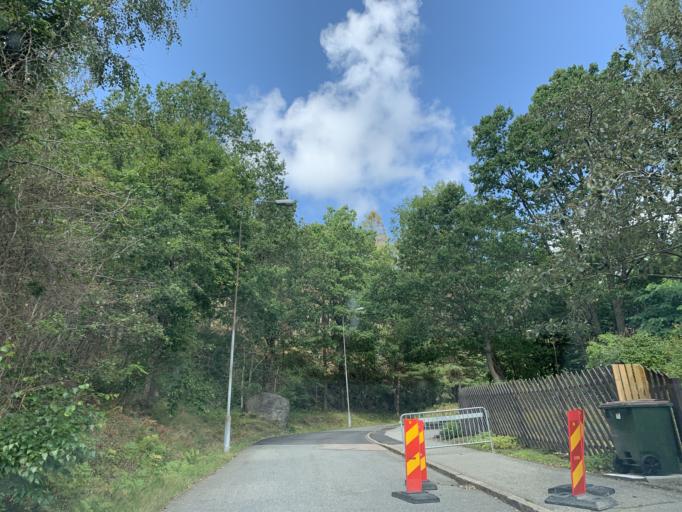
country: SE
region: Vaestra Goetaland
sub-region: Goteborg
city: Hammarkullen
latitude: 57.7736
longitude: 12.0325
